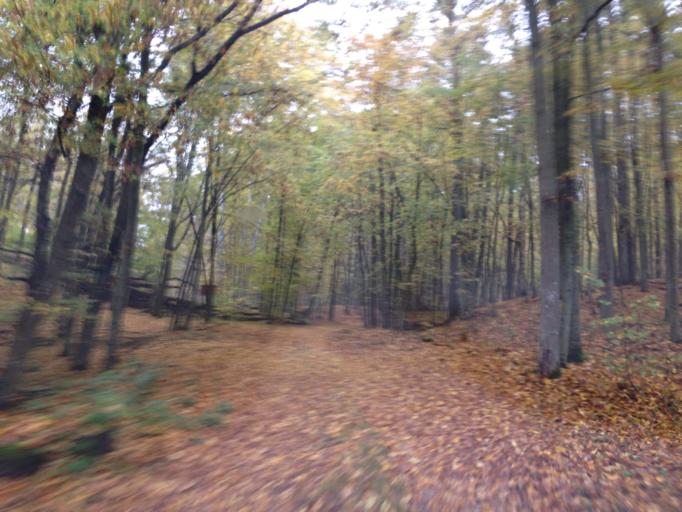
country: PL
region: Kujawsko-Pomorskie
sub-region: Powiat brodnicki
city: Gorzno
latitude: 53.2329
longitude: 19.7203
